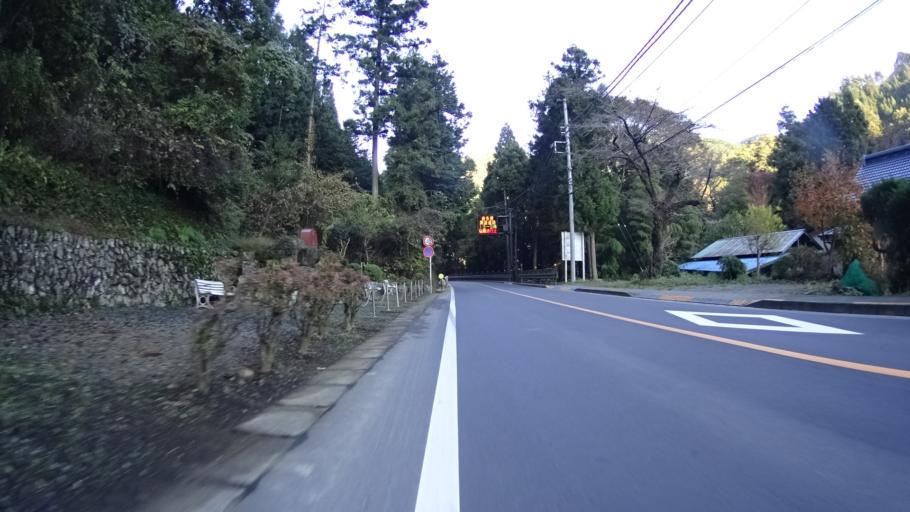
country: JP
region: Tokyo
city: Itsukaichi
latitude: 35.7237
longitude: 139.1727
